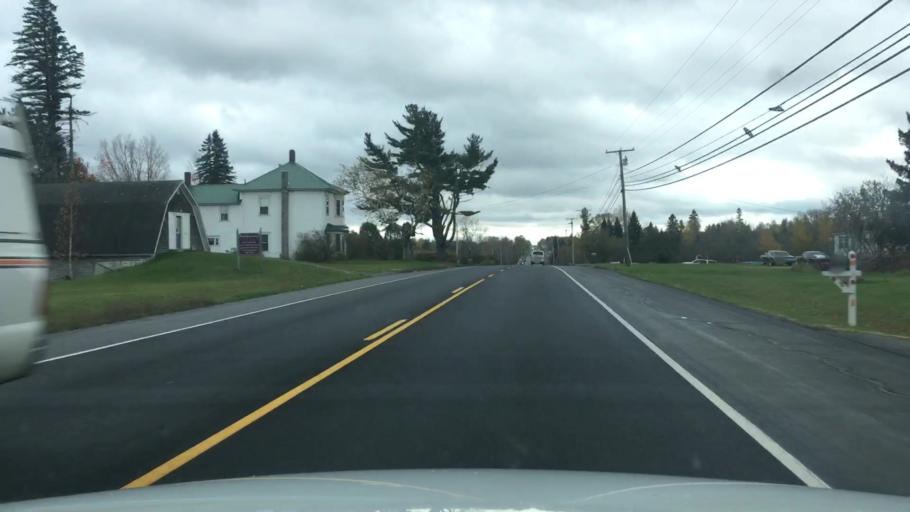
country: US
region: Maine
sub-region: Aroostook County
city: Houlton
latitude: 46.2490
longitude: -67.8408
